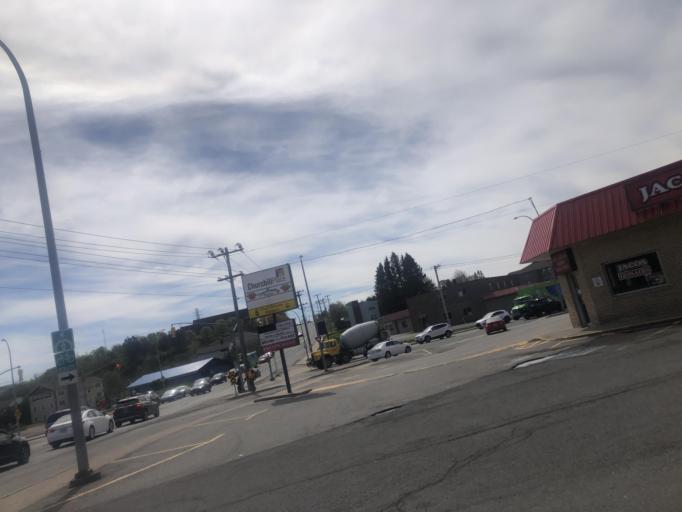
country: CA
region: New Brunswick
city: Saint John
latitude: 45.2872
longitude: -66.0794
